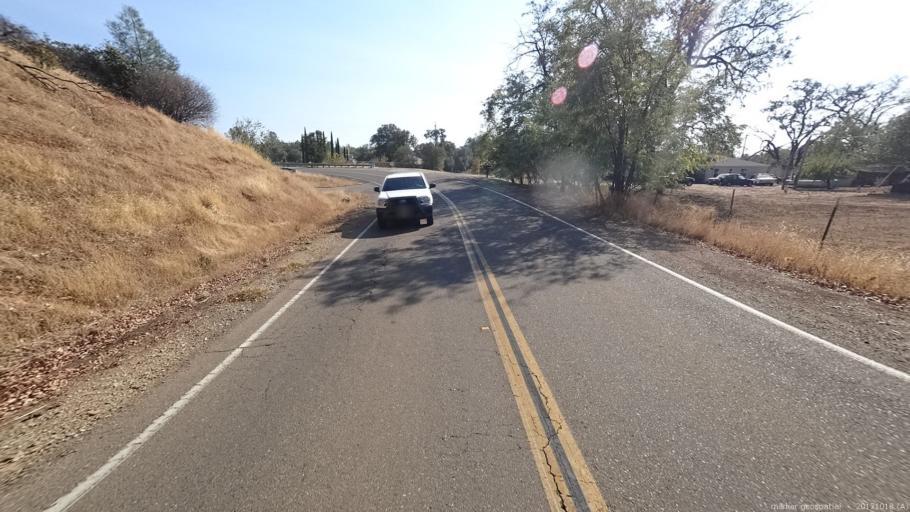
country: US
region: California
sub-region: Shasta County
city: Palo Cedro
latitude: 40.5612
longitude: -122.2844
